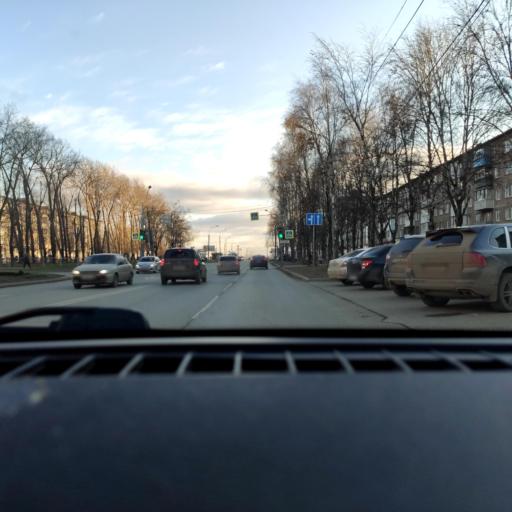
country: RU
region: Perm
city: Kondratovo
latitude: 57.9637
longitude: 56.1784
